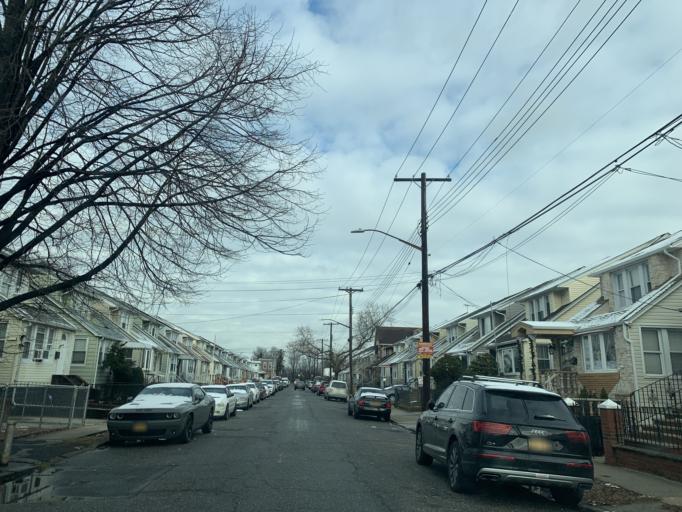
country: US
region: New York
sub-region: Queens County
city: Jamaica
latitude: 40.6854
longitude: -73.7762
